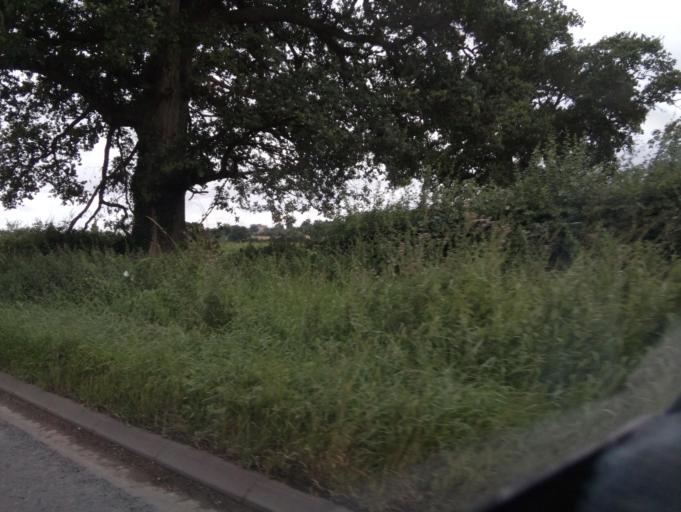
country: GB
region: England
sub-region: Worcestershire
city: Fernhill Heath
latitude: 52.2335
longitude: -2.1717
